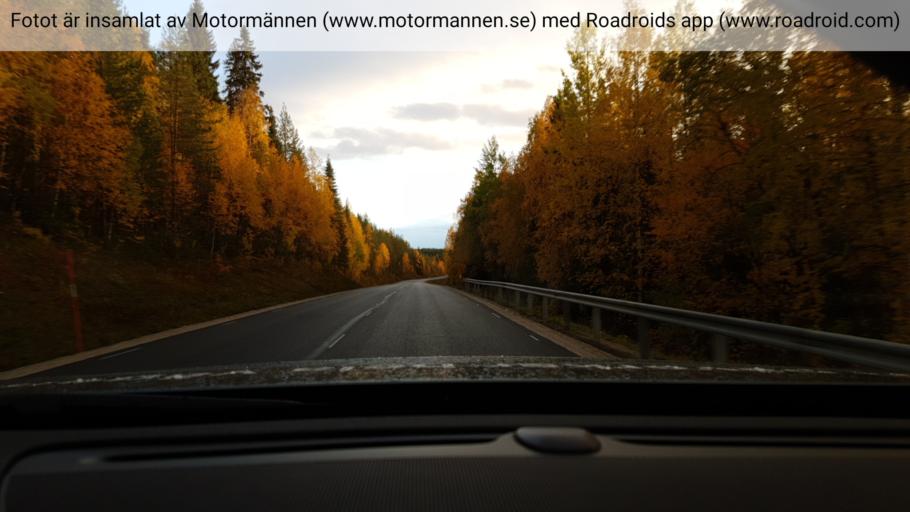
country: SE
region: Norrbotten
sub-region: Overkalix Kommun
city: OEverkalix
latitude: 66.4658
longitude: 22.7927
